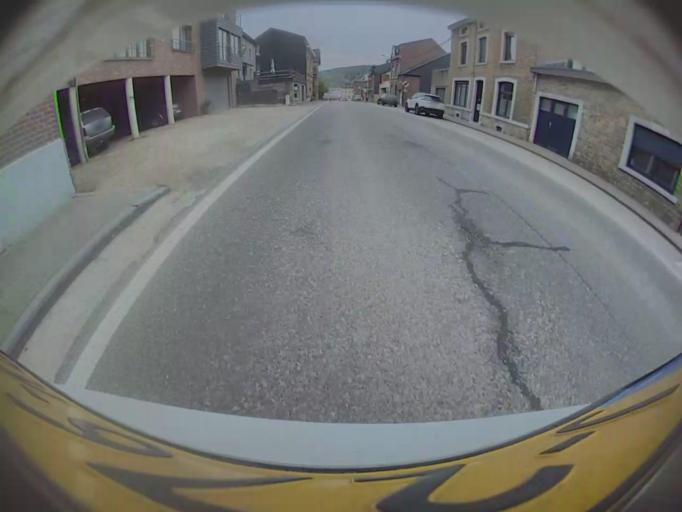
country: BE
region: Wallonia
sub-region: Province de Liege
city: Hamoir
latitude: 50.4268
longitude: 5.5307
